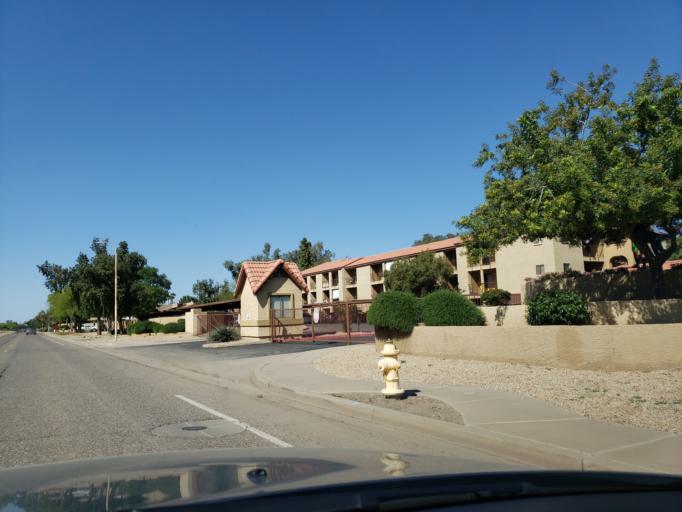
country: US
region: Arizona
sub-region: Maricopa County
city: Glendale
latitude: 33.5550
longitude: -112.1949
